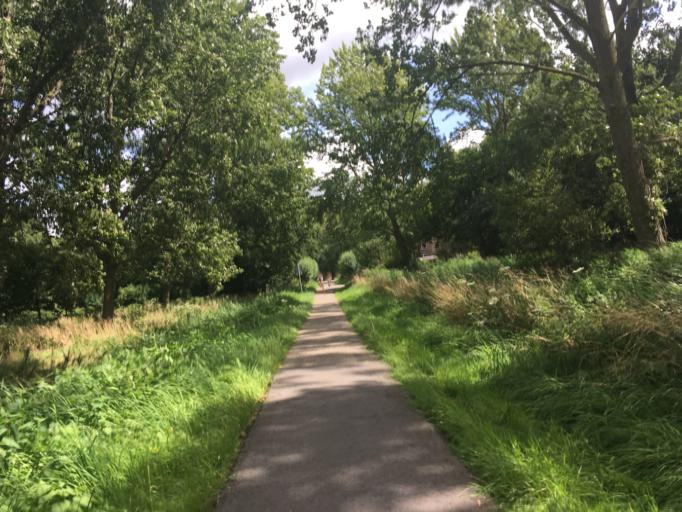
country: NL
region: North Holland
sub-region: Gemeente Haarlem
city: Haarlem
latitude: 52.3995
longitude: 4.7263
